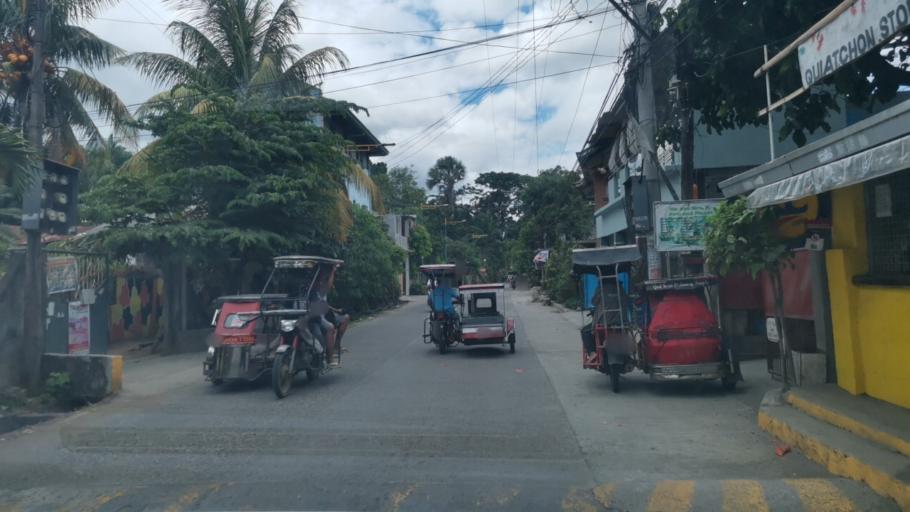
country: PH
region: Calabarzon
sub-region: Province of Batangas
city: Tanauan
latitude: 14.0892
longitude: 121.1397
